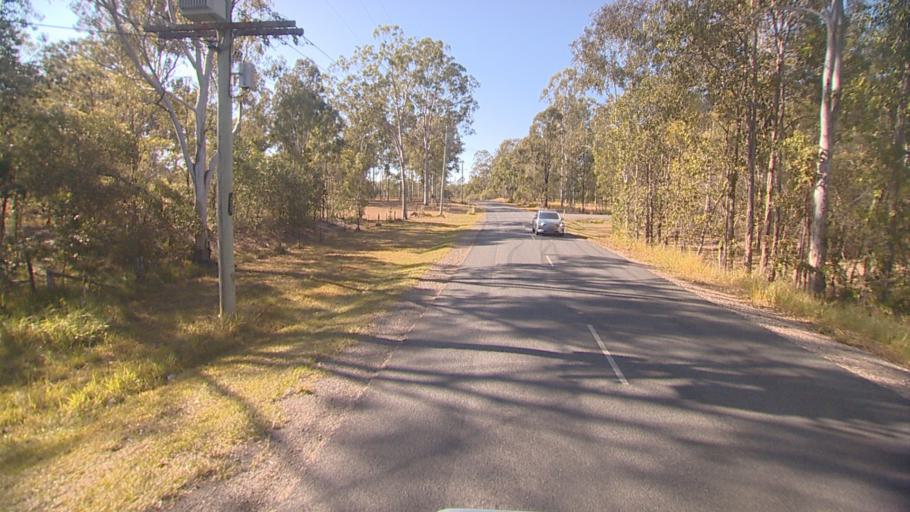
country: AU
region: Queensland
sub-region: Logan
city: Cedar Vale
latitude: -27.8424
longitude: 153.0394
